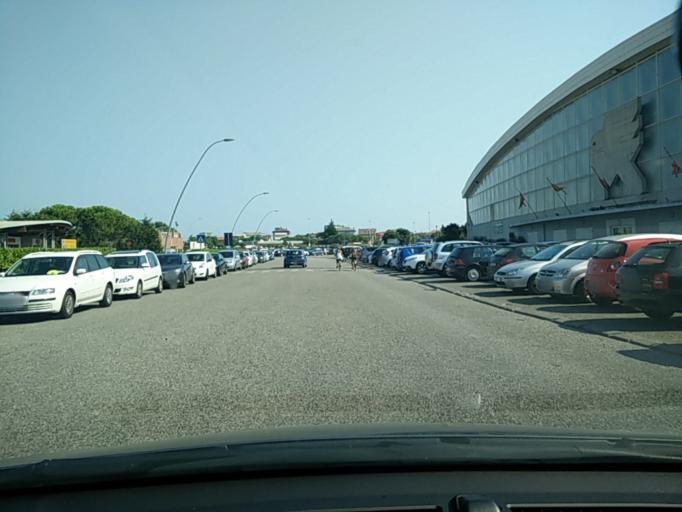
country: IT
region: Veneto
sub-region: Provincia di Venezia
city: Caorle
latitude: 45.6053
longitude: 12.8824
